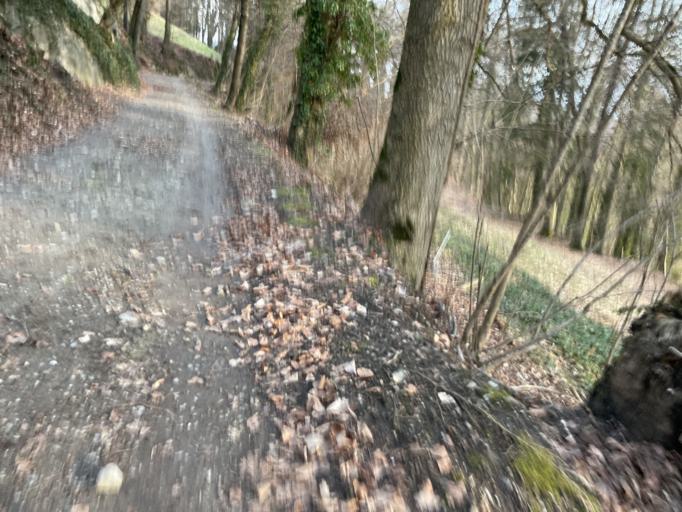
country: CH
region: Bern
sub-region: Bern-Mittelland District
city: Toffen
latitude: 46.8467
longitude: 7.5135
